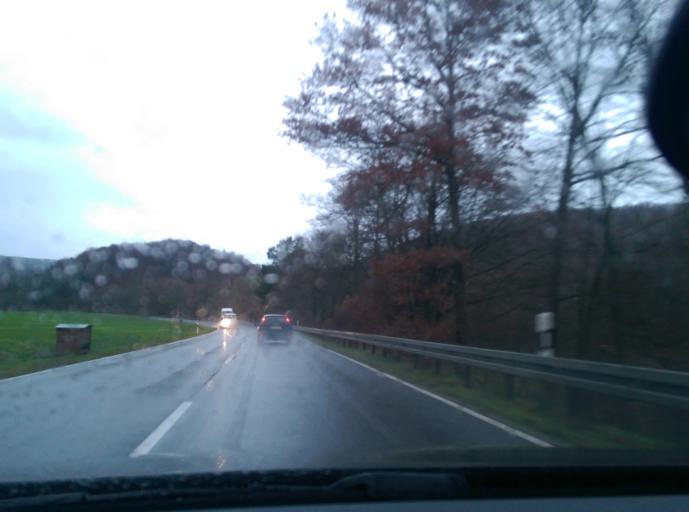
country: DE
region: Thuringia
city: Gerstungen
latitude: 51.0247
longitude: 10.0275
